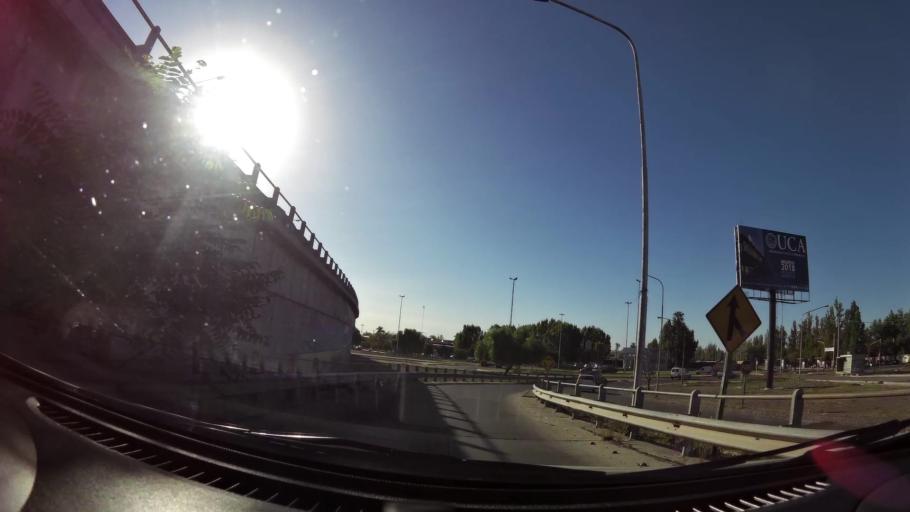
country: AR
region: Mendoza
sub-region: Departamento de Godoy Cruz
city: Godoy Cruz
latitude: -32.9259
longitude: -68.8337
